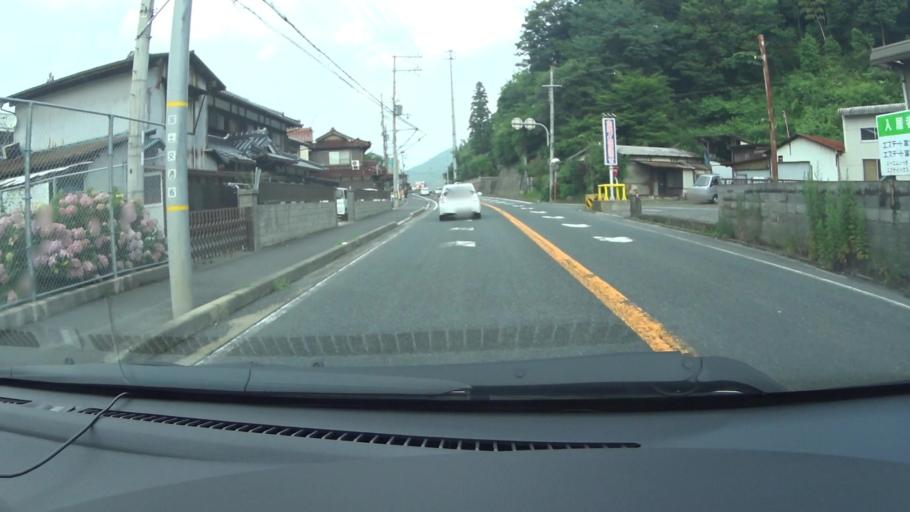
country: JP
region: Kyoto
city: Kameoka
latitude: 34.9897
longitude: 135.6063
